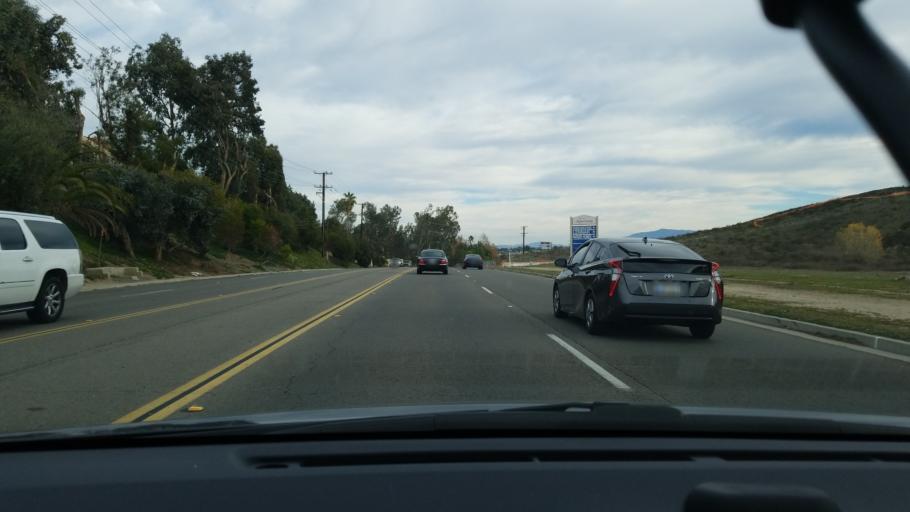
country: US
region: California
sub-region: Riverside County
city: Murrieta Hot Springs
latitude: 33.5549
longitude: -117.1471
